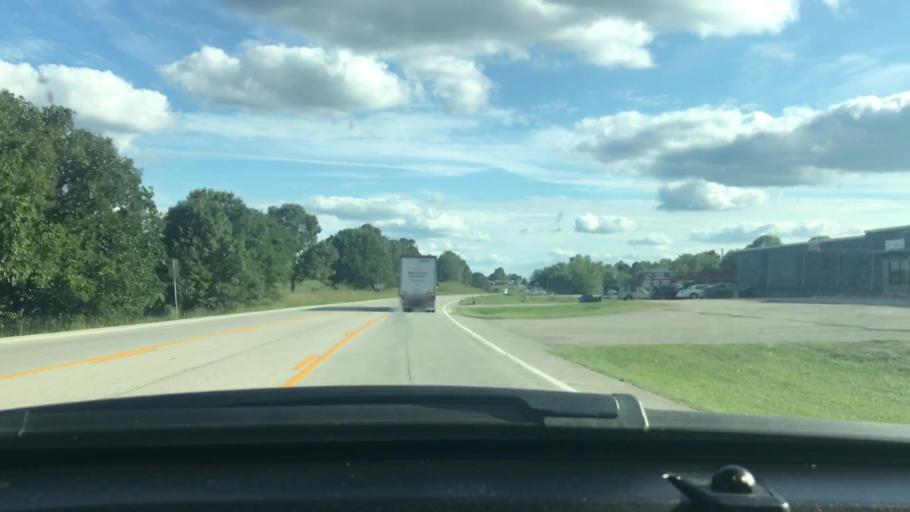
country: US
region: Missouri
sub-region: Oregon County
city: Thayer
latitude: 36.6040
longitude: -91.6442
